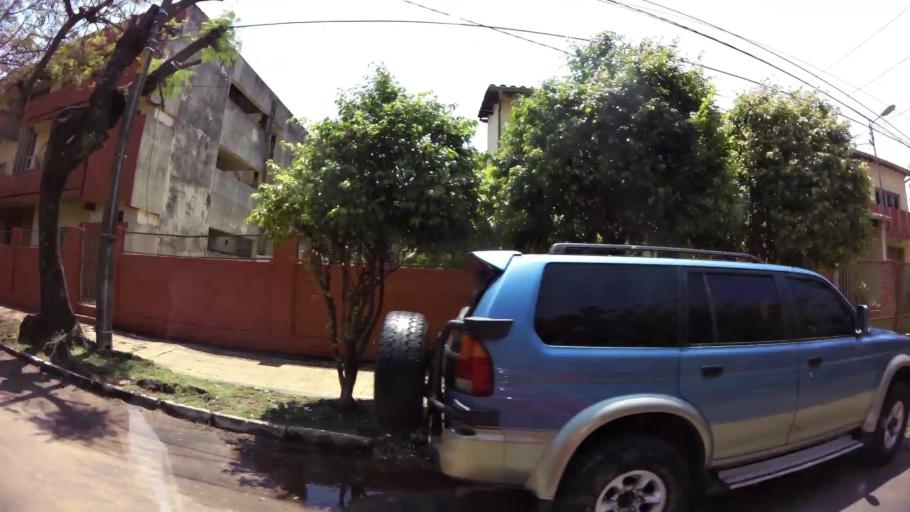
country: PY
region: Asuncion
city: Asuncion
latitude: -25.3040
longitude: -57.6540
